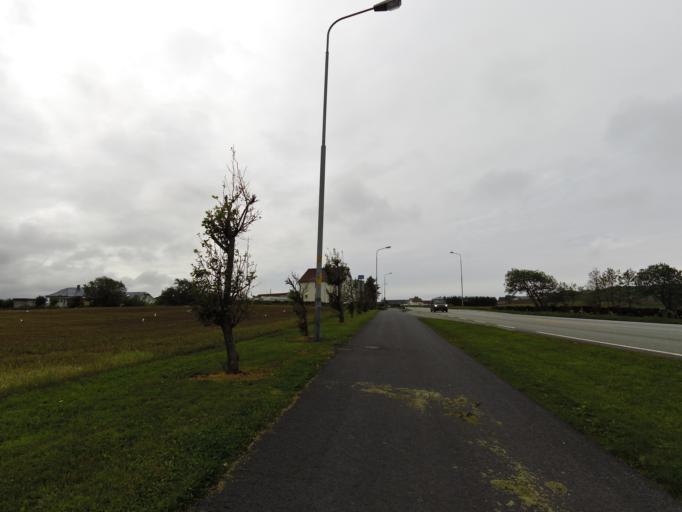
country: NO
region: Rogaland
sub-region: Klepp
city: Kleppe
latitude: 58.8292
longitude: 5.5934
